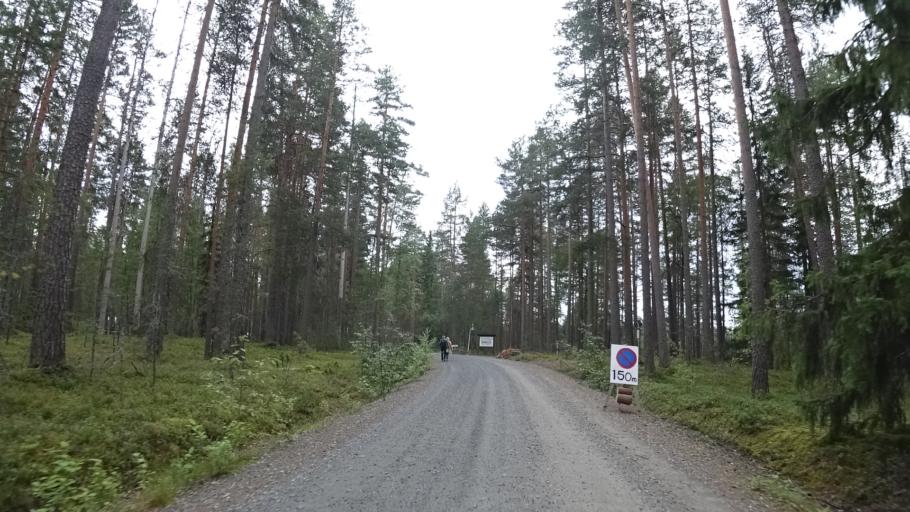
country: FI
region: North Karelia
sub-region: Joensuu
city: Ilomantsi
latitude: 62.5804
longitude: 31.1742
